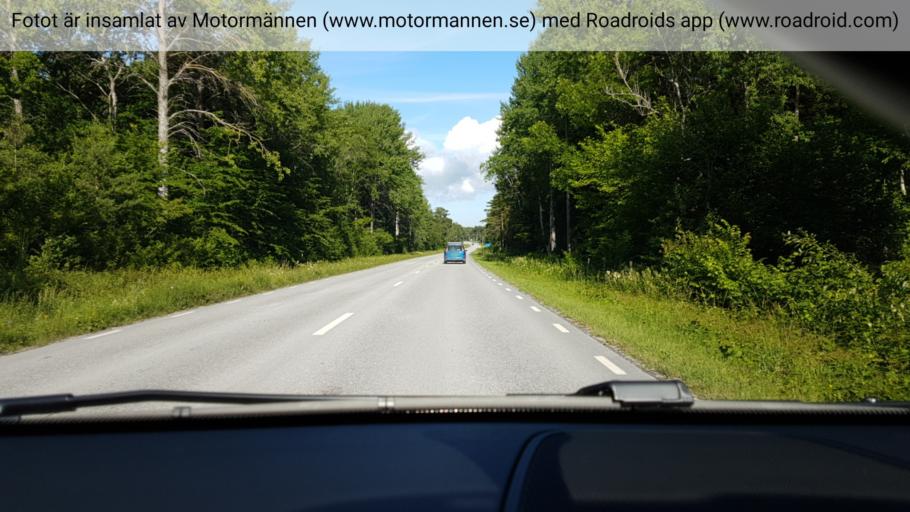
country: SE
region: Gotland
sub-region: Gotland
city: Slite
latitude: 57.7496
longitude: 18.7175
